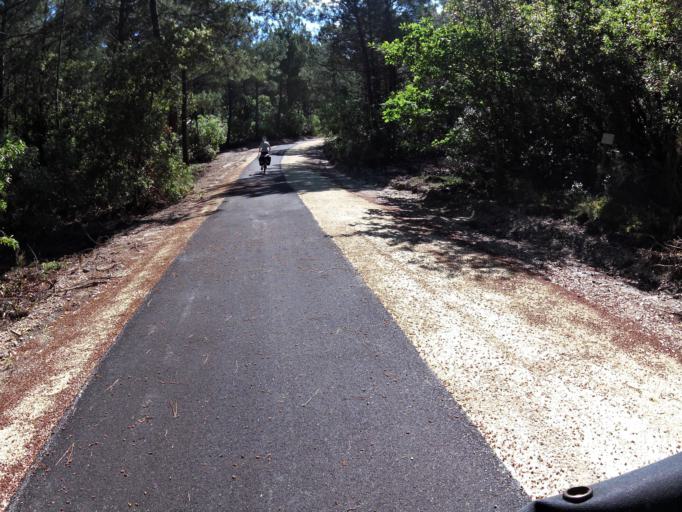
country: FR
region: Aquitaine
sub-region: Departement de la Gironde
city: Lacanau
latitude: 45.0317
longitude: -1.1631
